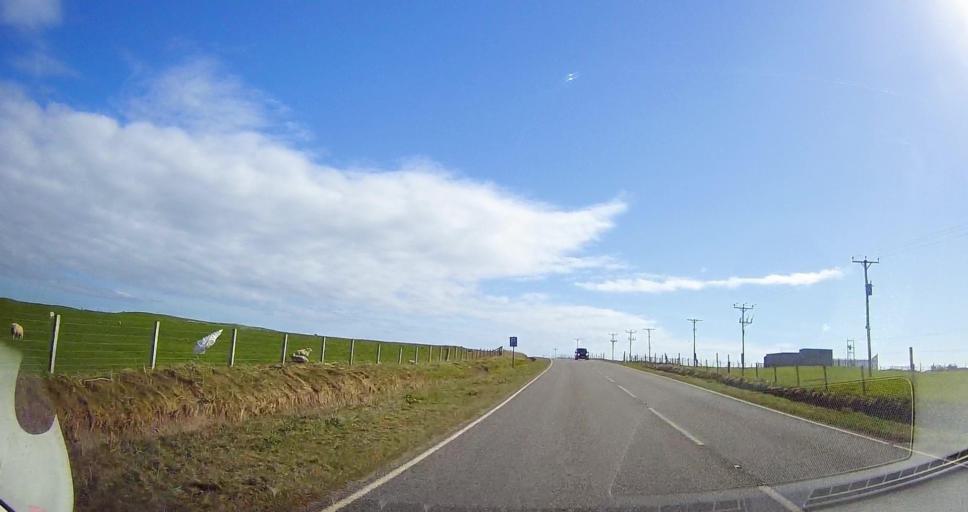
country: GB
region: Scotland
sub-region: Shetland Islands
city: Sandwick
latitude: 59.8997
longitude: -1.3034
